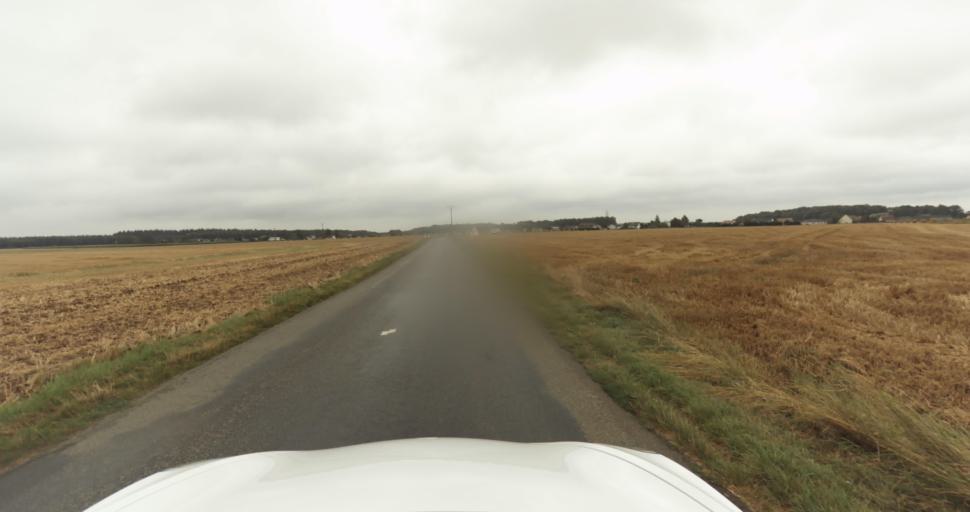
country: FR
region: Haute-Normandie
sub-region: Departement de l'Eure
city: Aviron
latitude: 49.0655
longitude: 1.1197
